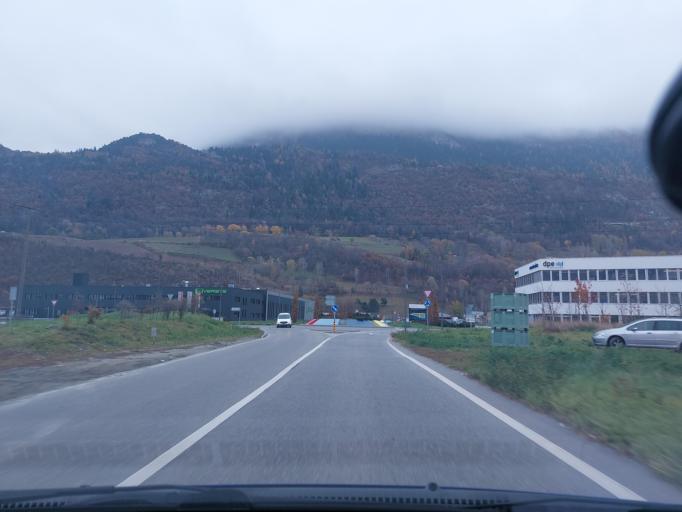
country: CH
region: Valais
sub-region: Sierre District
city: Chalais
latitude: 46.2744
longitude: 7.5172
